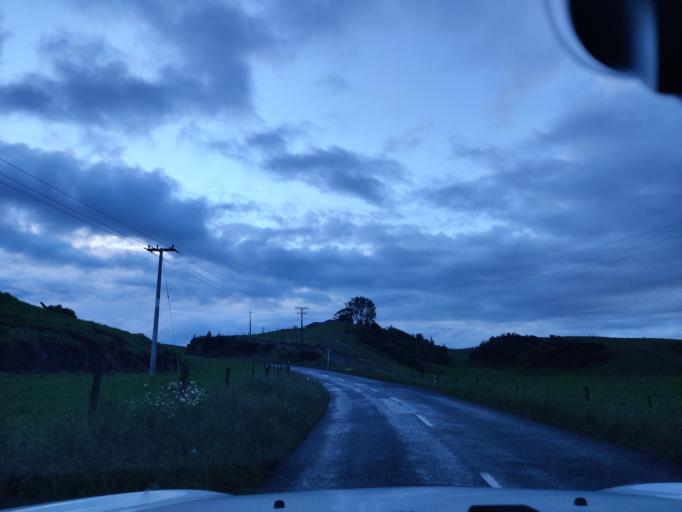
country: NZ
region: Waikato
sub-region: South Waikato District
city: Tokoroa
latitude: -38.1812
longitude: 175.7826
